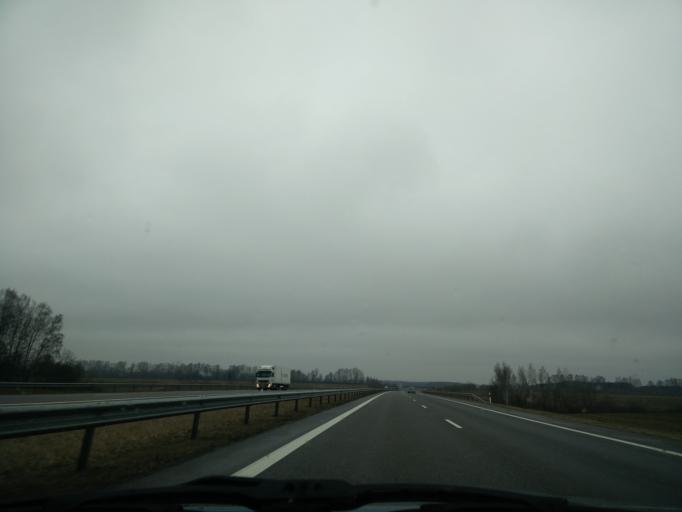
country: LT
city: Skaudvile
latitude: 55.4035
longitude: 22.8486
